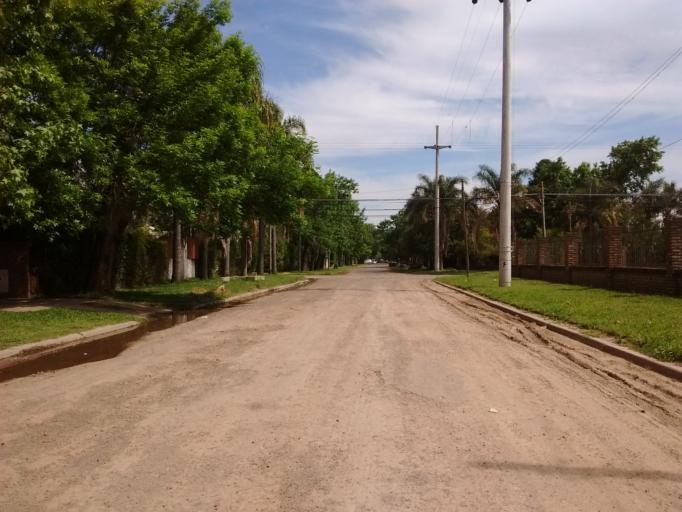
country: AR
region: Santa Fe
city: Funes
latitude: -32.9145
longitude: -60.8028
